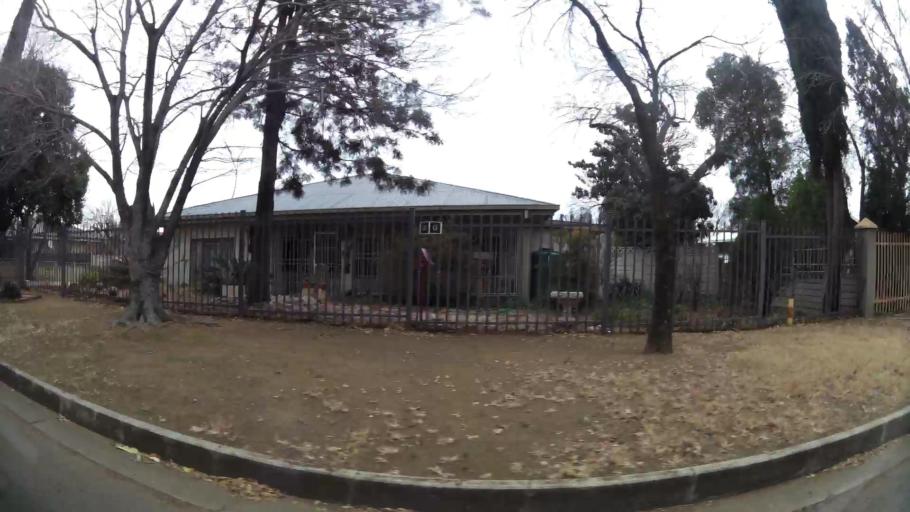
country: ZA
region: Orange Free State
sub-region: Fezile Dabi District Municipality
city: Kroonstad
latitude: -27.6858
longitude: 27.2376
